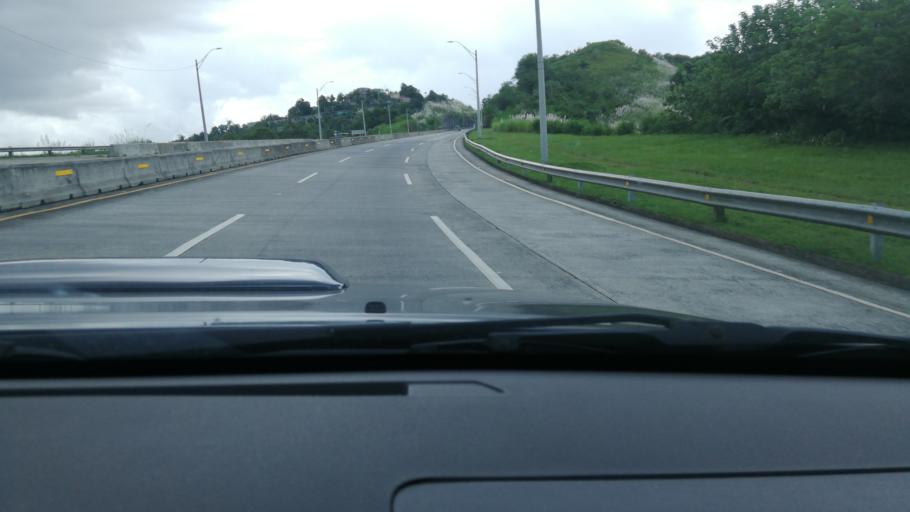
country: PA
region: Panama
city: San Miguelito
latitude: 9.0658
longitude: -79.4744
